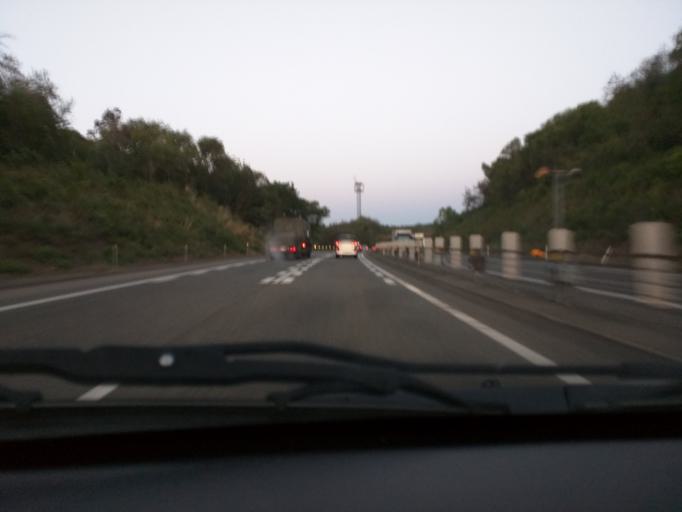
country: JP
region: Niigata
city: Kashiwazaki
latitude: 37.3483
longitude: 138.5069
